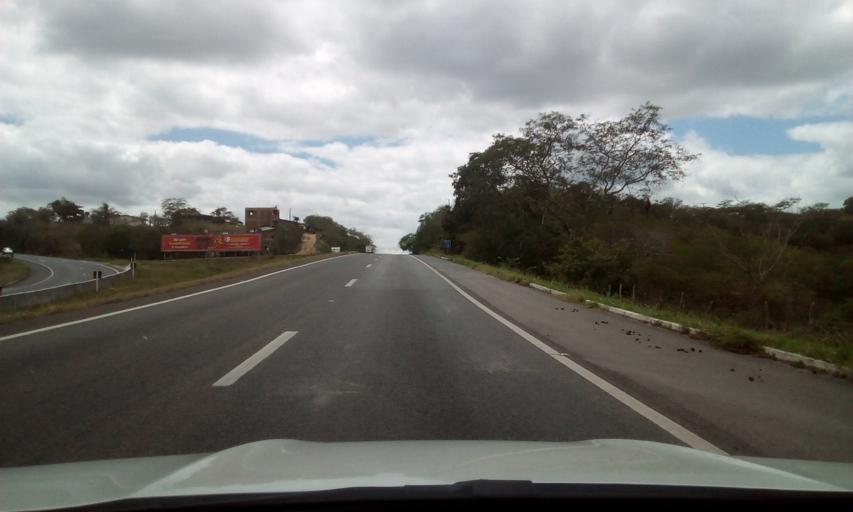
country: BR
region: Paraiba
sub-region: Inga
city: Inga
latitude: -7.2607
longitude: -35.6976
